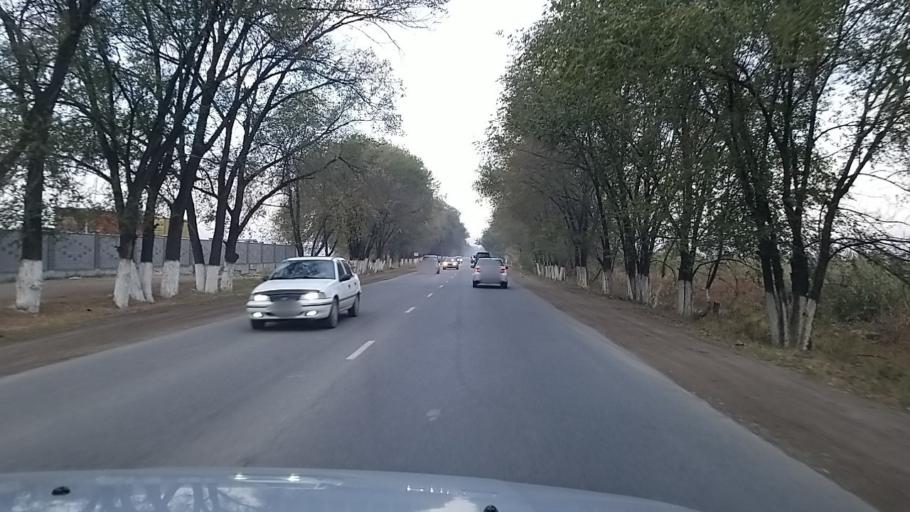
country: KZ
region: Almaty Oblysy
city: Burunday
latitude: 43.3581
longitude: 76.7777
